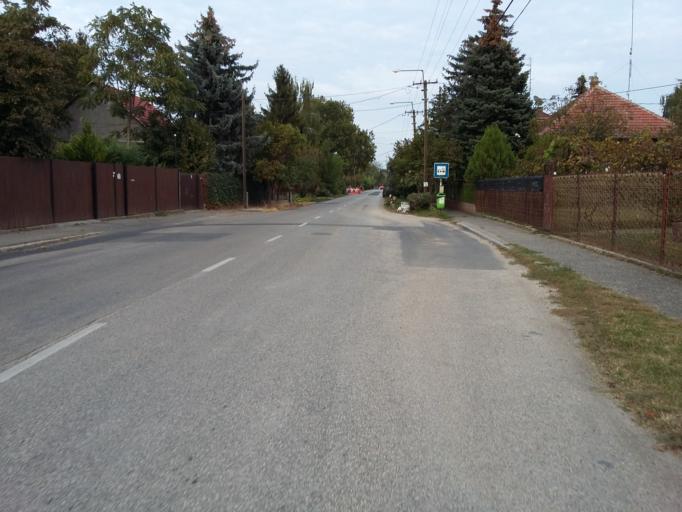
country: HU
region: Csongrad
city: Szeged
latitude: 46.2265
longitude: 20.1127
